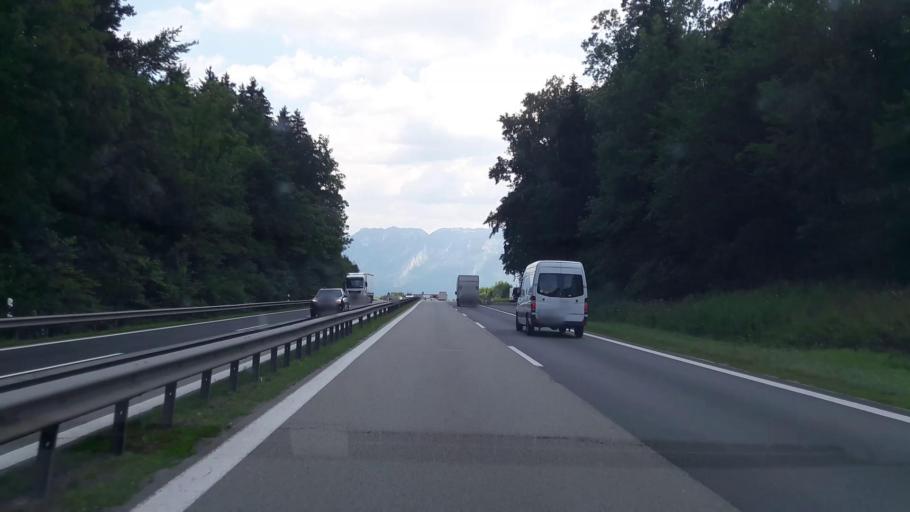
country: DE
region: Bavaria
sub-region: Upper Bavaria
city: Anger
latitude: 47.8098
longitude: 12.8382
